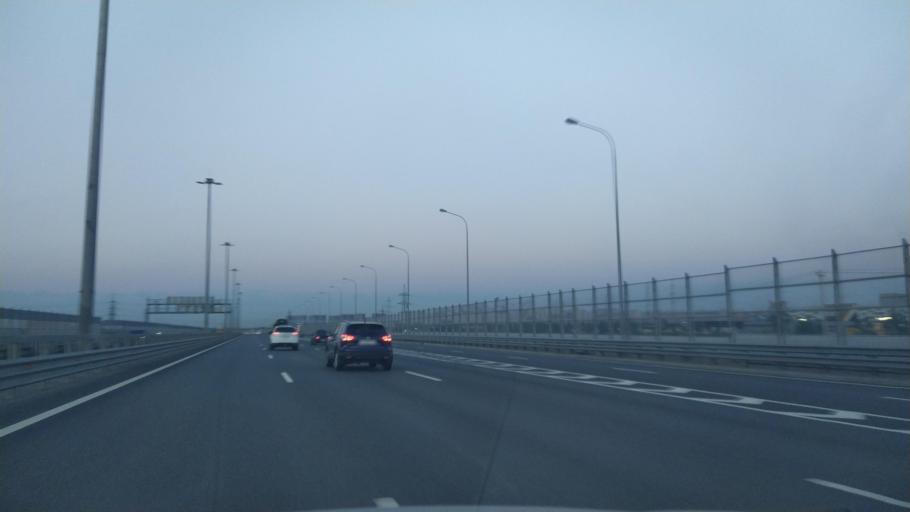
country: RU
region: St.-Petersburg
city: Pargolovo
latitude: 60.0979
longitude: 30.3003
